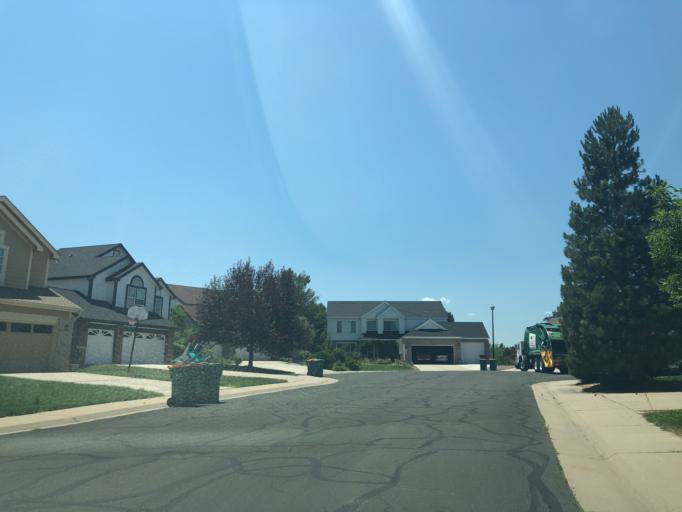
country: US
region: Colorado
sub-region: Arapahoe County
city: Dove Valley
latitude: 39.6265
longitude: -104.7671
